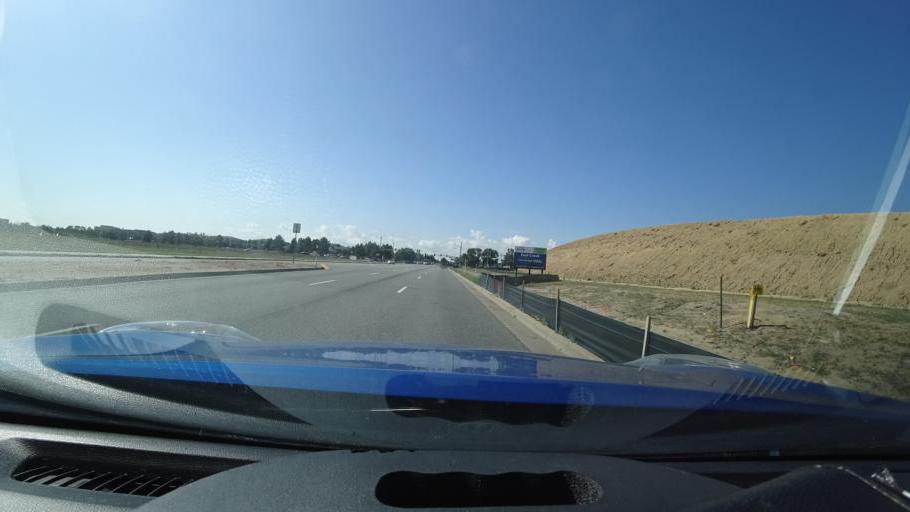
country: US
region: Colorado
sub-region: Adams County
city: Aurora
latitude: 39.7083
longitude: -104.7912
